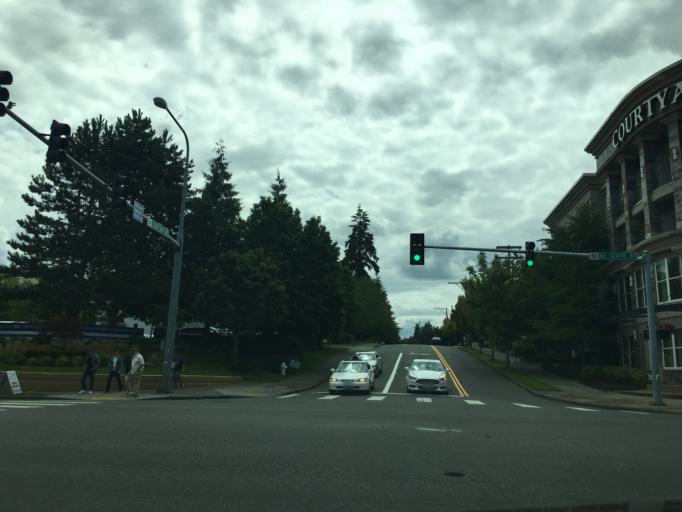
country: US
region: Washington
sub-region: King County
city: Kingsgate
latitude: 47.7113
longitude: -122.1905
